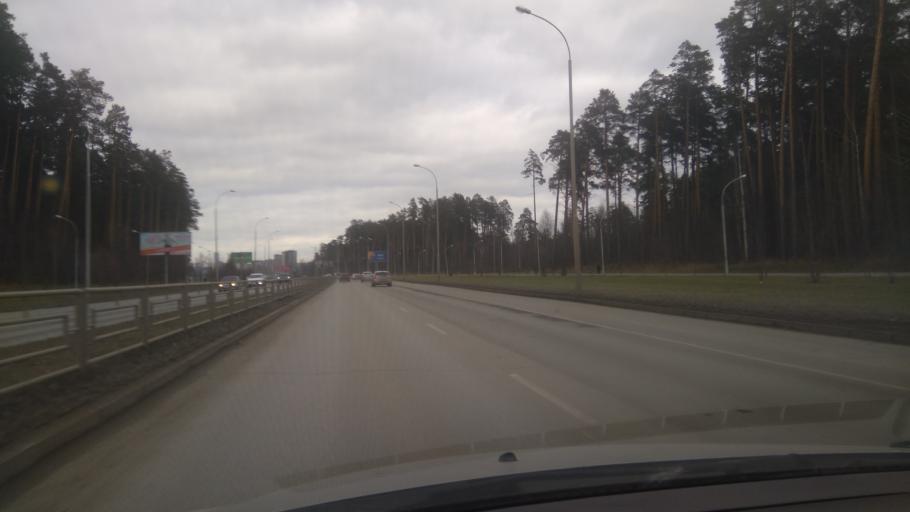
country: RU
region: Sverdlovsk
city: Sovkhoznyy
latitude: 56.7983
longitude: 60.5311
